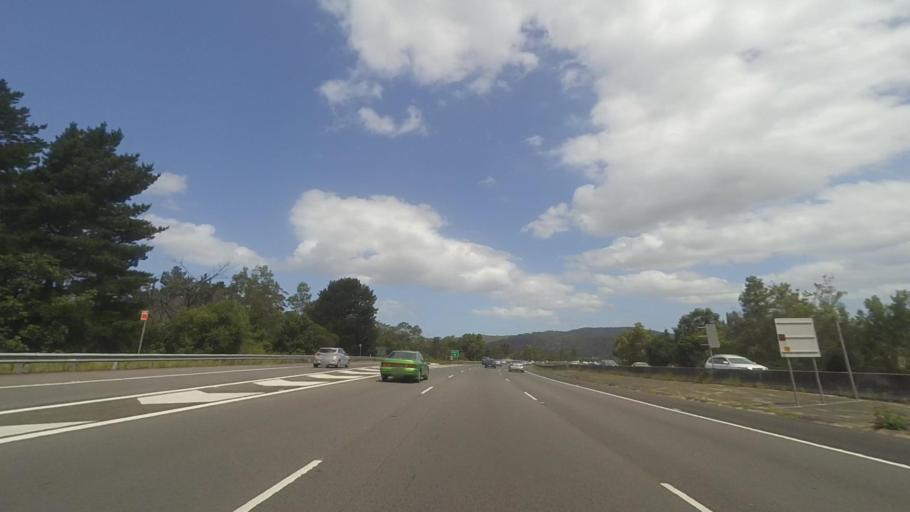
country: AU
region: New South Wales
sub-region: Hornsby Shire
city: Berowra Heights
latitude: -33.5275
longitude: 151.1987
